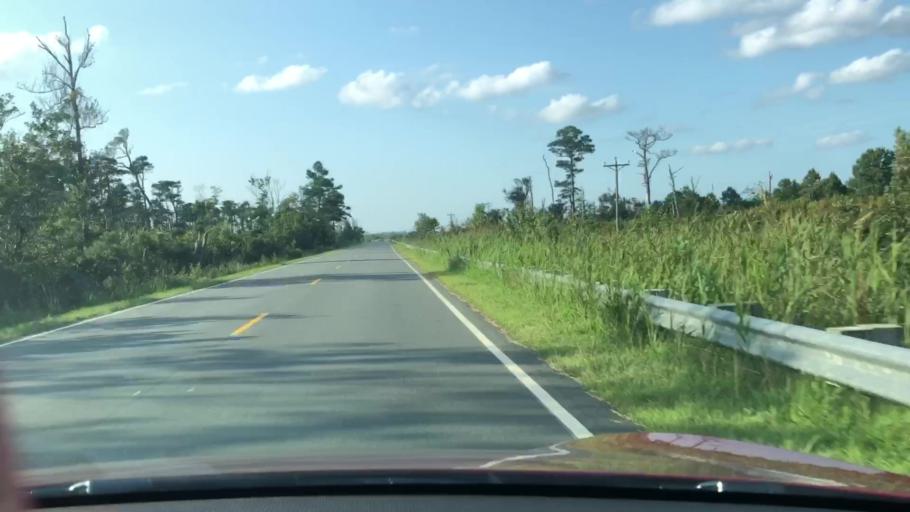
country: US
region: North Carolina
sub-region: Dare County
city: Wanchese
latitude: 35.6782
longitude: -75.7796
